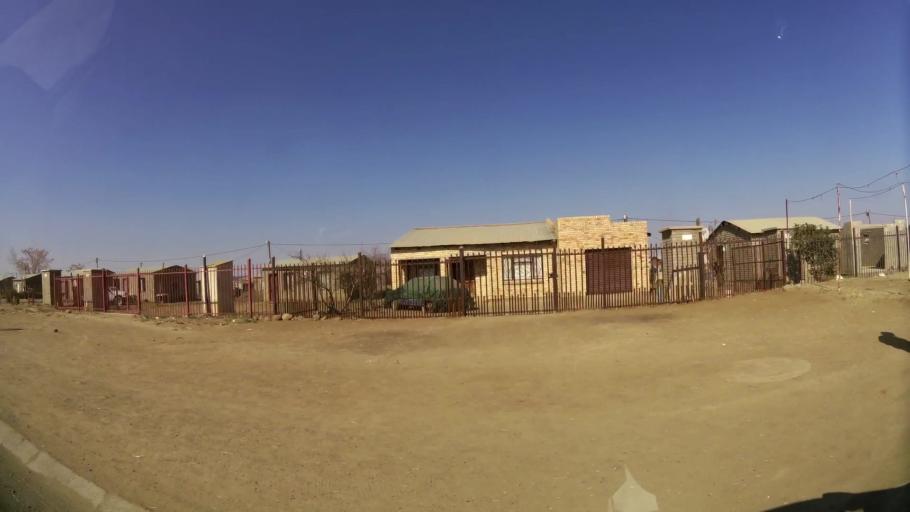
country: ZA
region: Orange Free State
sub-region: Mangaung Metropolitan Municipality
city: Bloemfontein
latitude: -29.1950
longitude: 26.2748
